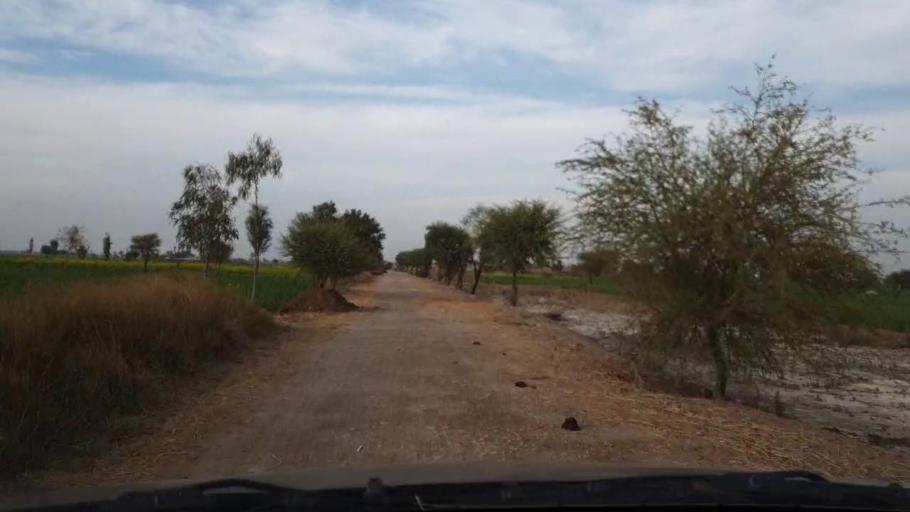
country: PK
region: Sindh
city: Khadro
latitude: 26.1553
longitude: 68.7358
